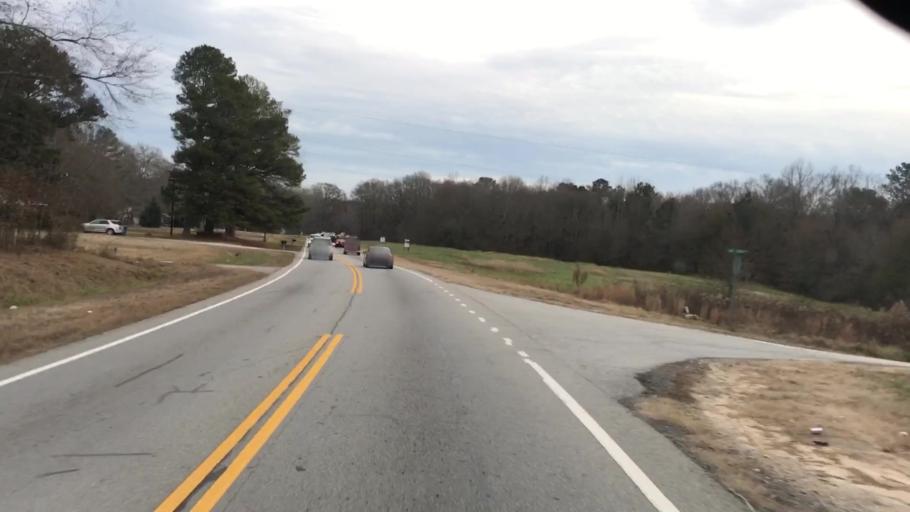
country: US
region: Georgia
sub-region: Jackson County
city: Hoschton
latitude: 34.0836
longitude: -83.7990
